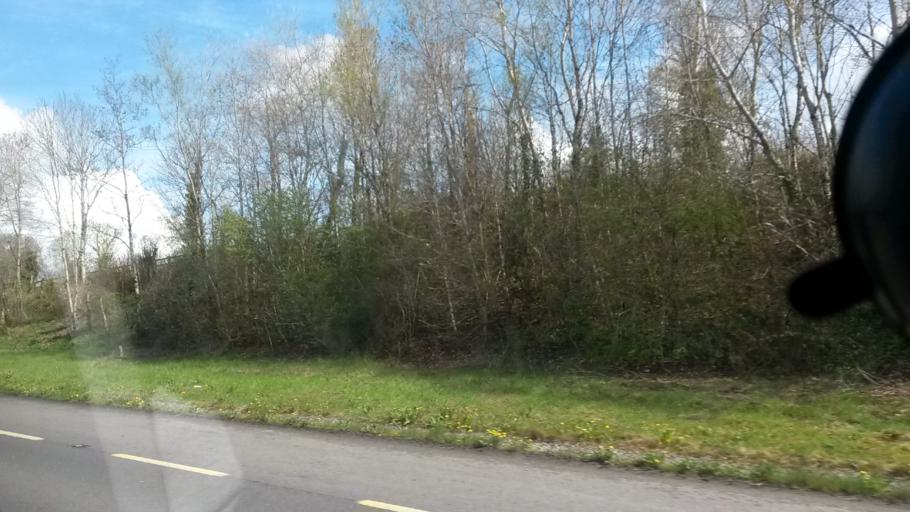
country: IE
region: Ulster
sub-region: An Cabhan
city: Belturbet
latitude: 54.1053
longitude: -7.4674
